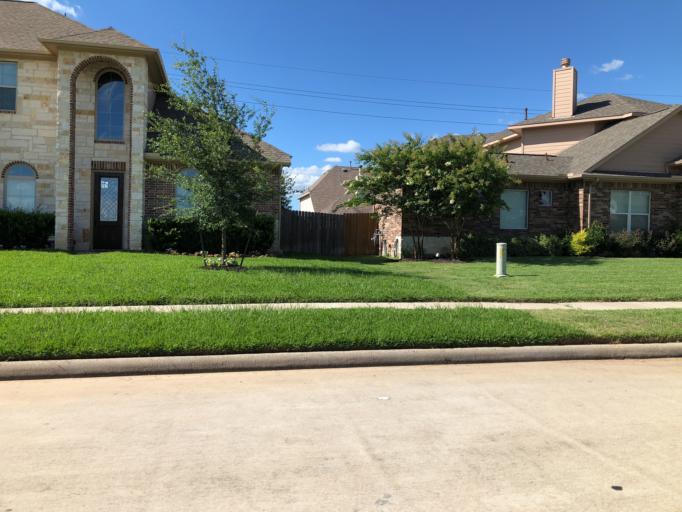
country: US
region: Texas
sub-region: Harris County
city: Katy
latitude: 29.8083
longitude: -95.8317
